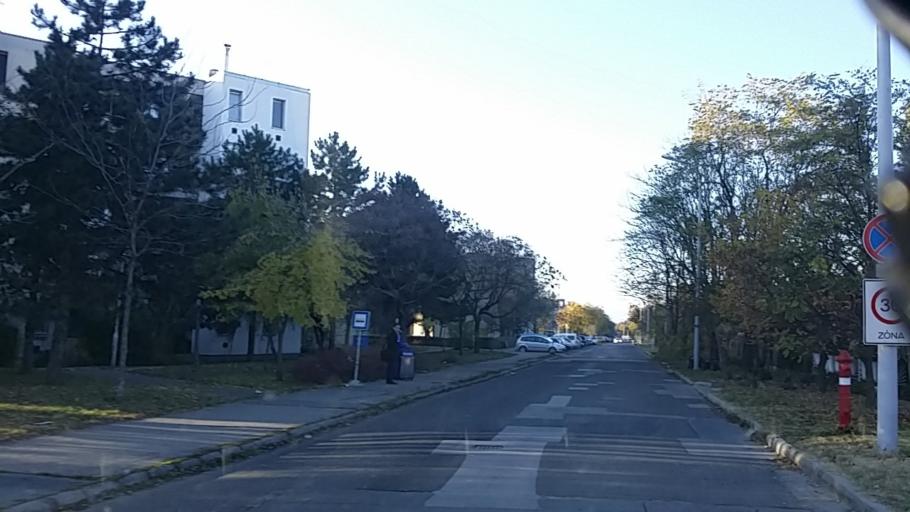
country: HU
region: Budapest
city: Budapest XVI. keruelet
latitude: 47.5165
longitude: 19.1885
